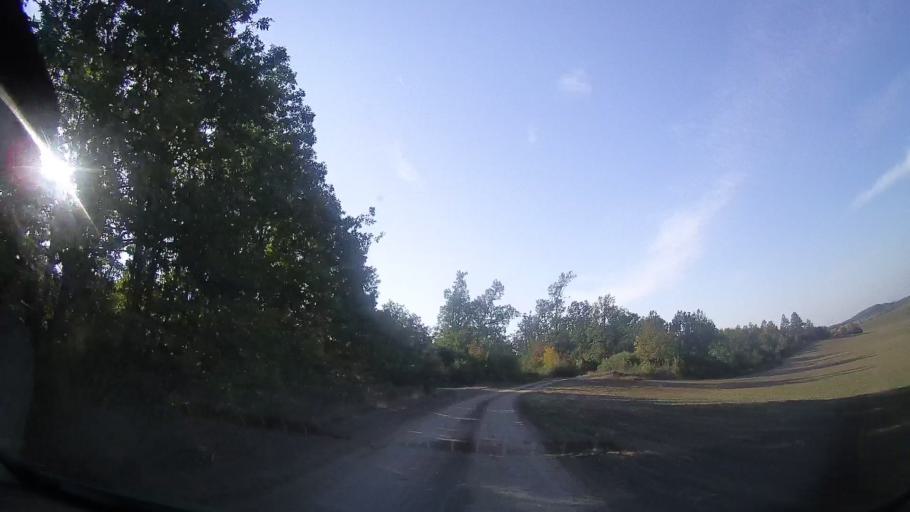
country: RO
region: Timis
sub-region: Comuna Bogda
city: Bogda
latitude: 45.9227
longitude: 21.6135
